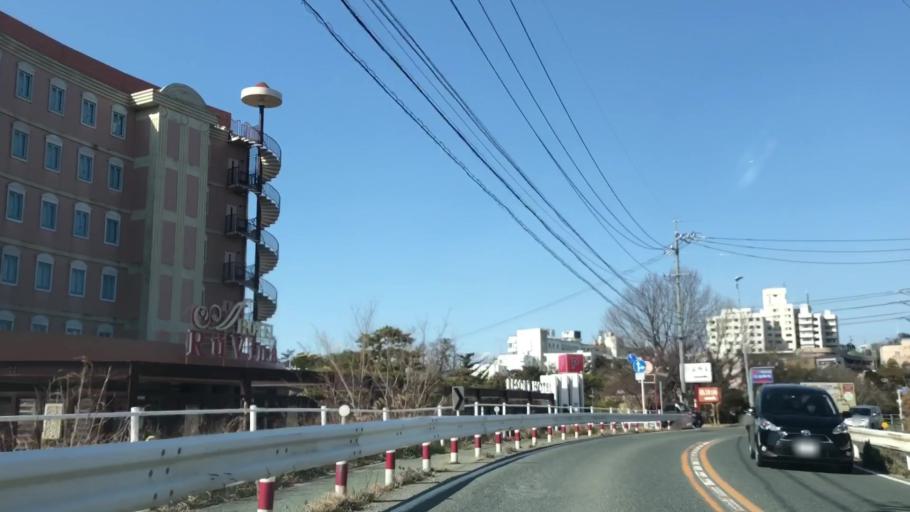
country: JP
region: Aichi
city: Gamagori
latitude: 34.8055
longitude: 137.2604
